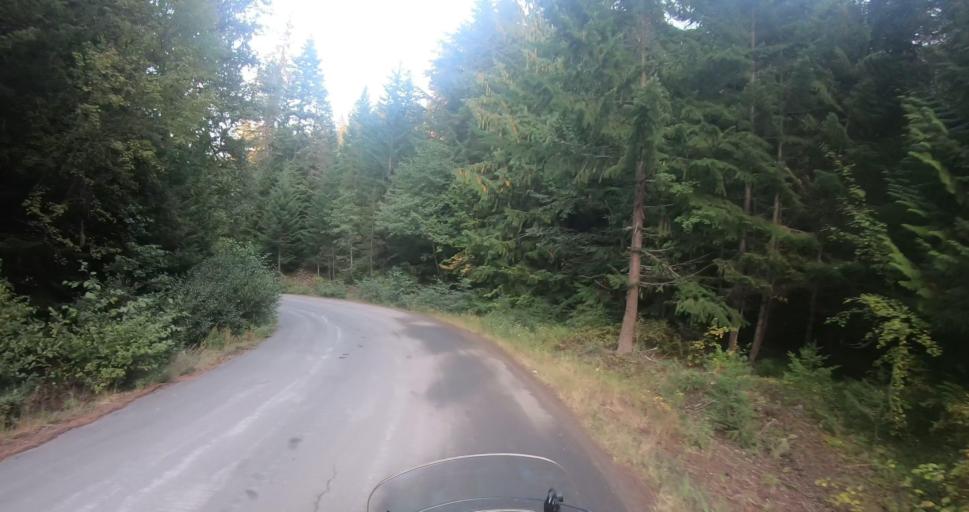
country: US
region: Oregon
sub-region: Hood River County
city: Odell
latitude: 45.4587
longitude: -121.6478
